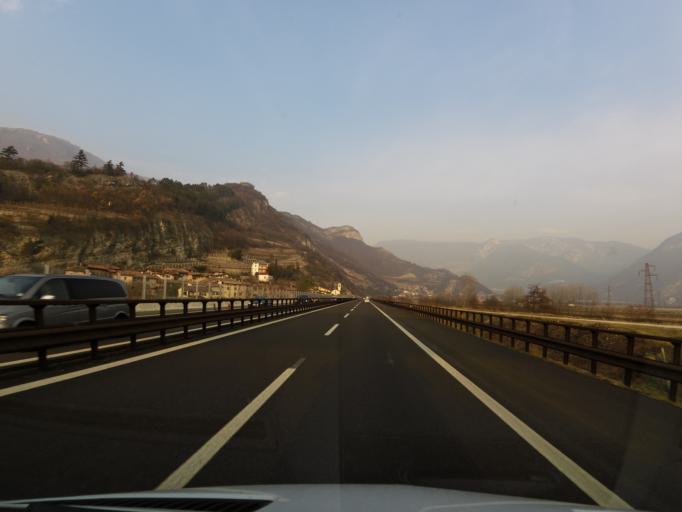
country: IT
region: Trentino-Alto Adige
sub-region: Provincia di Trento
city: Pomarolo
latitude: 45.9239
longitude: 11.0522
